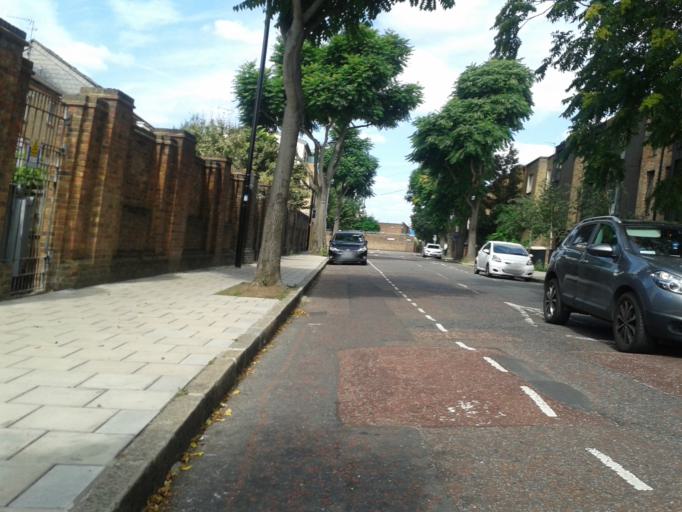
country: GB
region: England
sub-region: Greater London
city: Camberwell
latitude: 51.4907
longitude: -0.0741
